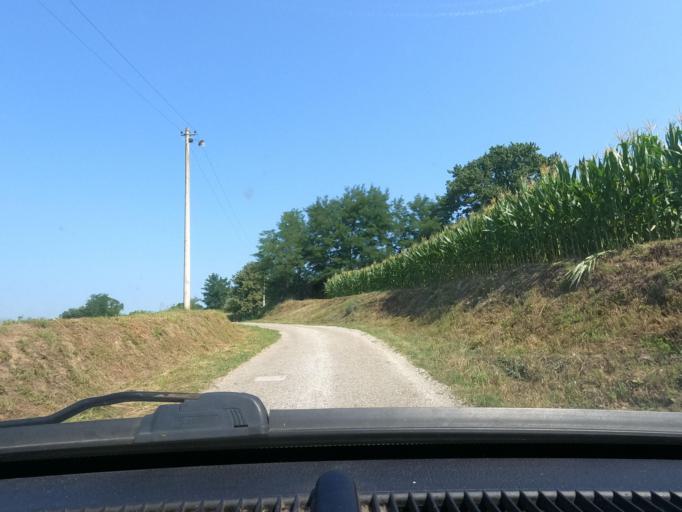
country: RS
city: Jarebice
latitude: 44.5410
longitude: 19.3766
